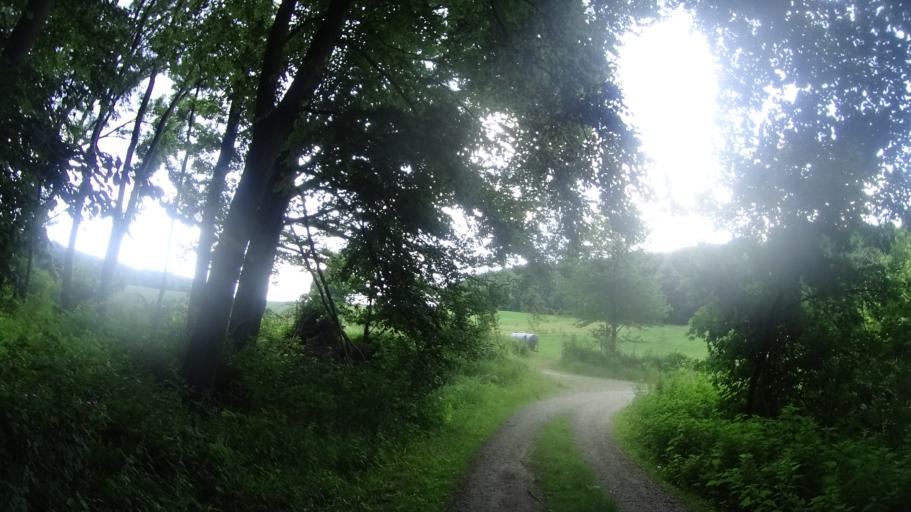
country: DE
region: Lower Saxony
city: Elbe
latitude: 52.0734
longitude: 10.3430
